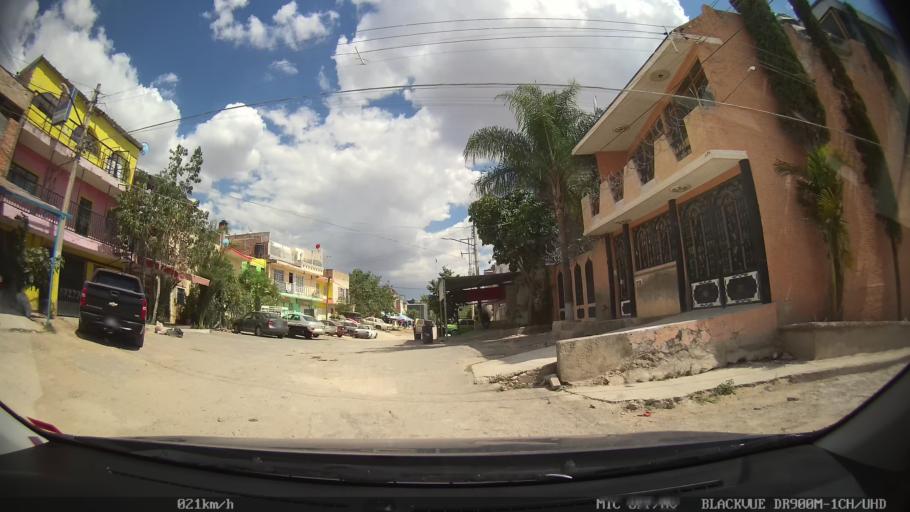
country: MX
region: Jalisco
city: Tlaquepaque
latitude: 20.6885
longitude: -103.2677
